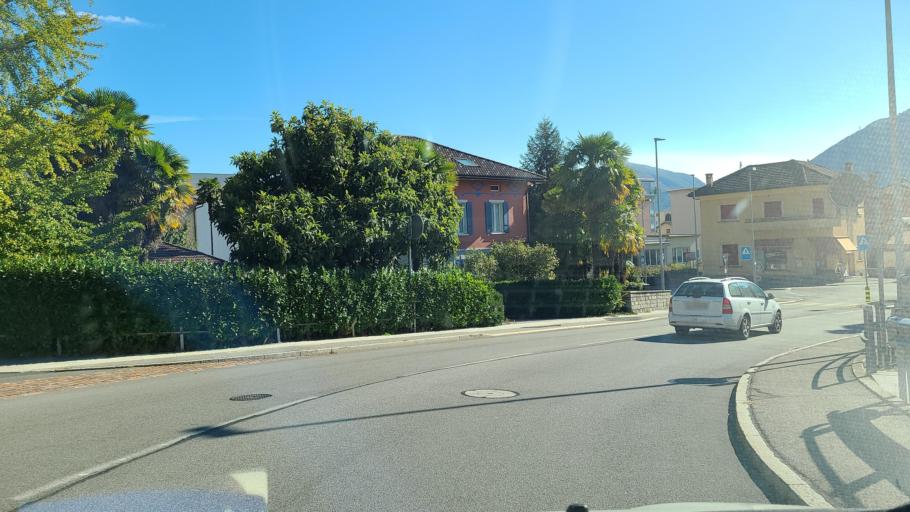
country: CH
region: Ticino
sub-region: Locarno District
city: Gordola
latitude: 46.1809
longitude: 8.8487
